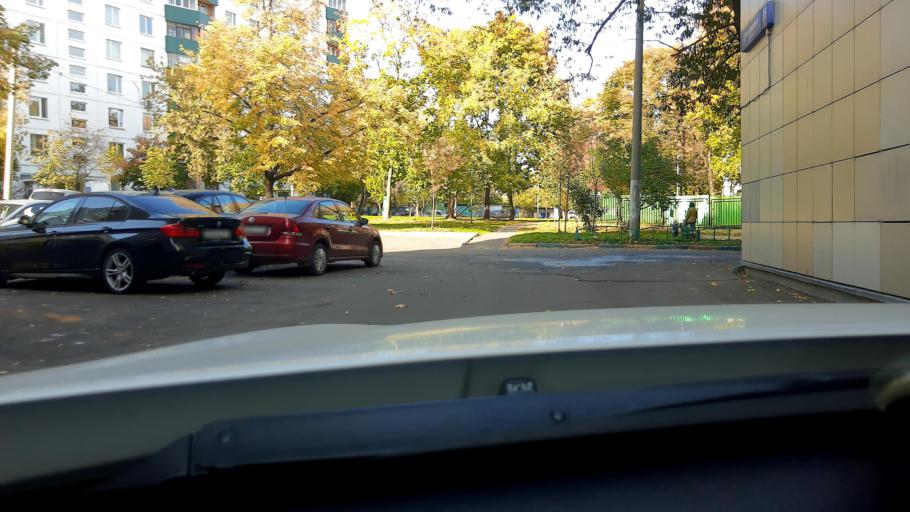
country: RU
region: Moscow
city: Likhobory
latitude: 55.8296
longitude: 37.5697
